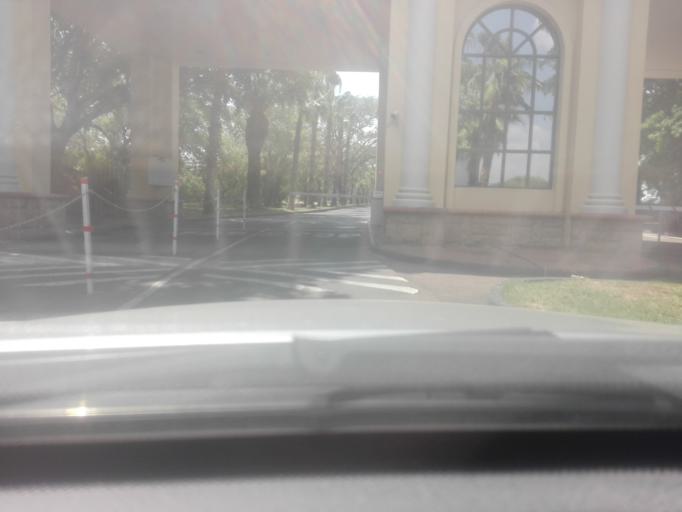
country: BW
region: Kweneng
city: Mogoditshane
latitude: -24.6411
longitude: 25.8796
